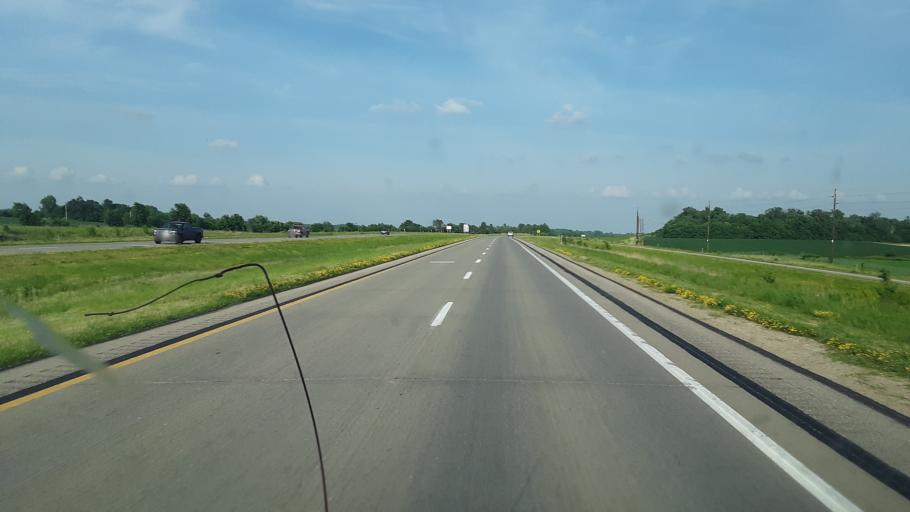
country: US
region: Iowa
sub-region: Marshall County
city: Marshalltown
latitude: 42.0118
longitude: -92.7844
